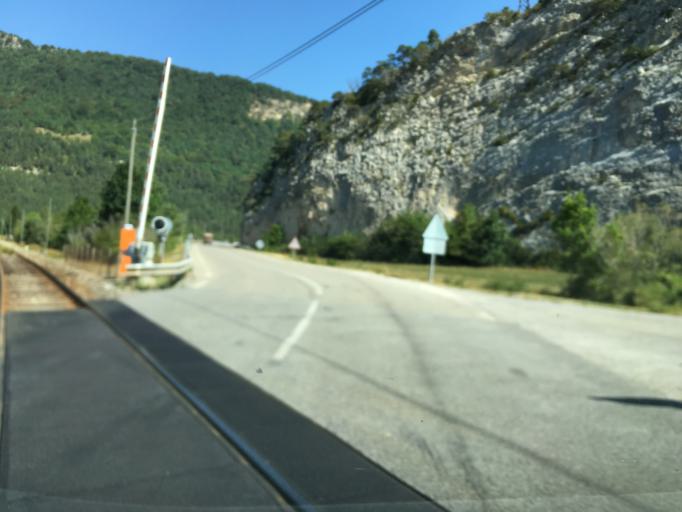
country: FR
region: Provence-Alpes-Cote d'Azur
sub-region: Departement des Hautes-Alpes
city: Veynes
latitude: 44.6368
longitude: 5.6957
